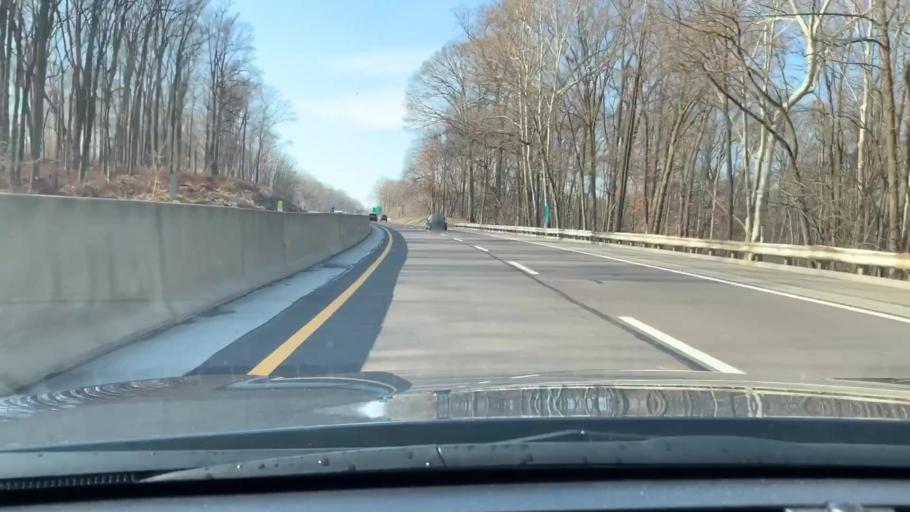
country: US
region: Pennsylvania
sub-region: Chester County
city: Chester Springs
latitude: 40.0654
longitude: -75.6386
